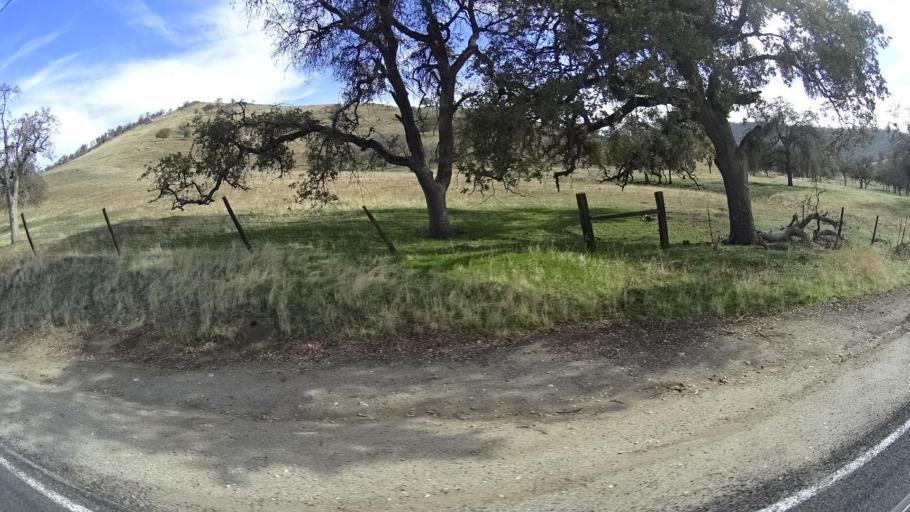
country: US
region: California
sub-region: Kern County
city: Alta Sierra
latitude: 35.6312
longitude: -118.8002
